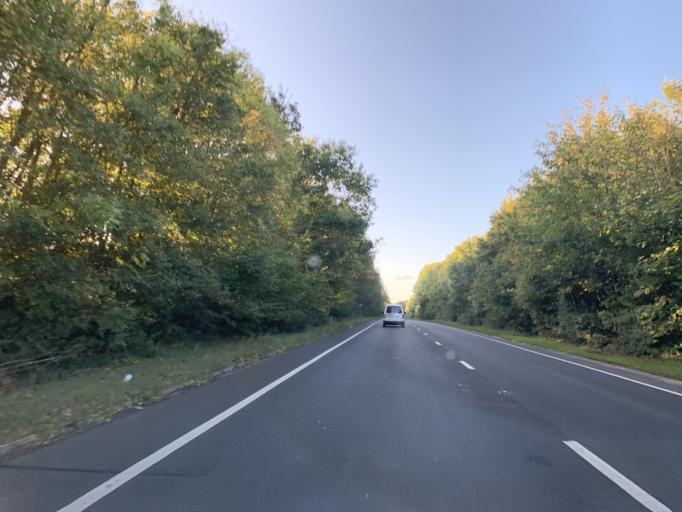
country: GB
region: England
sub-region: Wiltshire
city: Whiteparish
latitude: 51.0003
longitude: -1.6612
